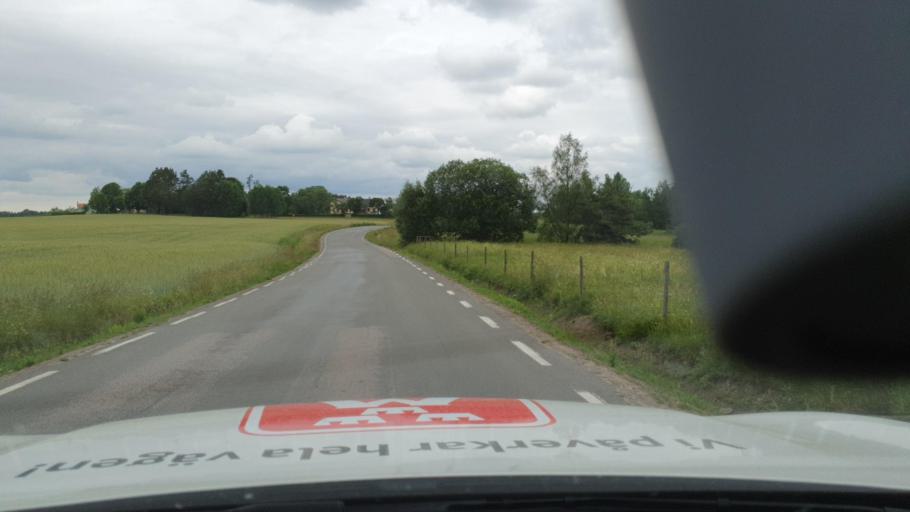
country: SE
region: Vaestra Goetaland
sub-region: Tidaholms Kommun
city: Olofstorp
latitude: 58.2302
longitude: 14.1019
